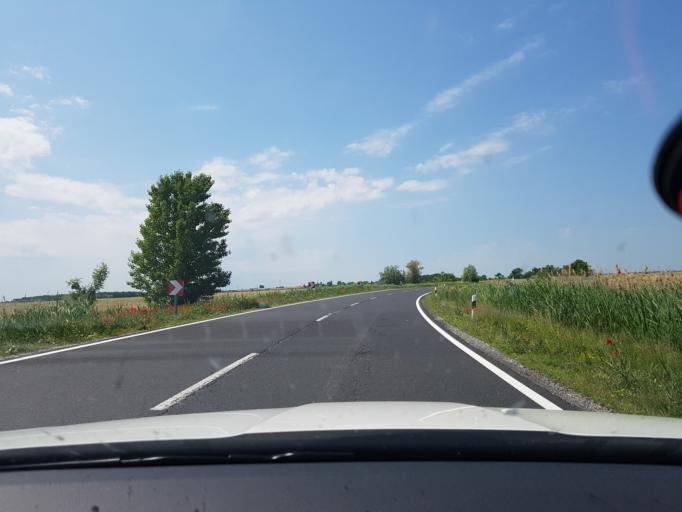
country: HU
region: Hajdu-Bihar
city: Egyek
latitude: 47.5503
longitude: 20.9519
